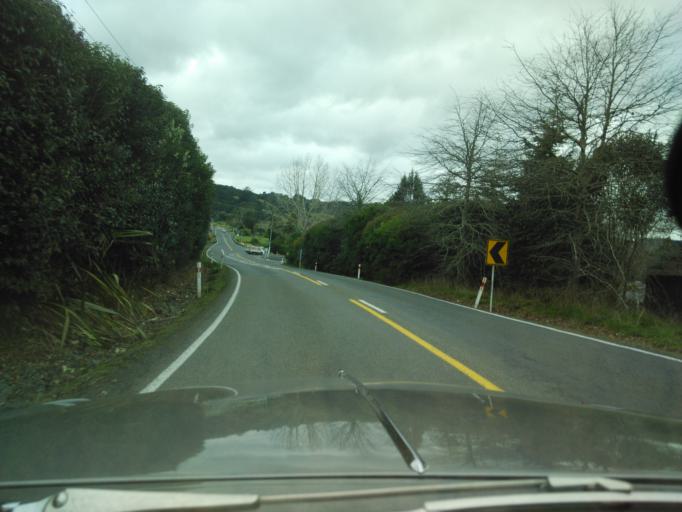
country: NZ
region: Auckland
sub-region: Auckland
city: Parakai
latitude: -36.6258
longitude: 174.5020
